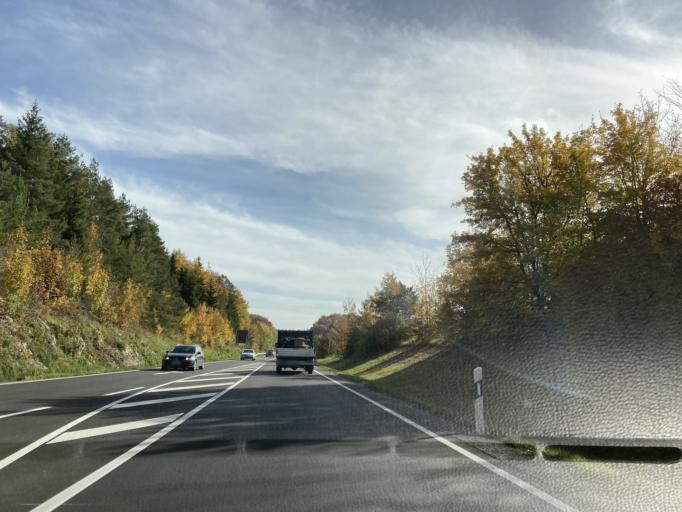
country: DE
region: Baden-Wuerttemberg
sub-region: Tuebingen Region
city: Winterlingen
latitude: 48.1389
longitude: 9.1554
